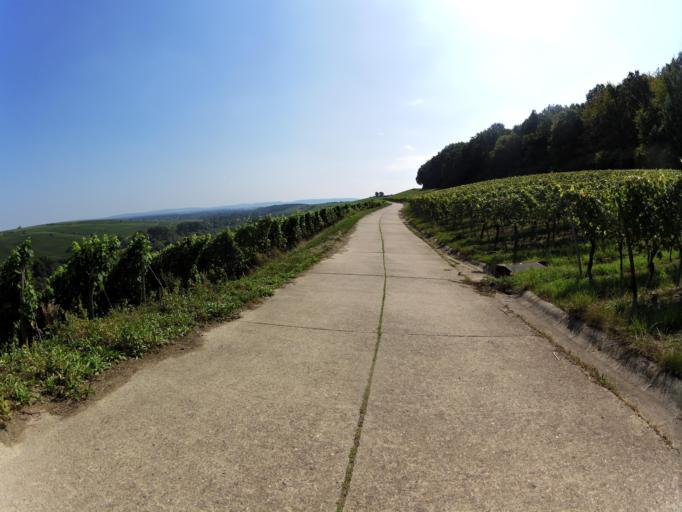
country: DE
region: Bavaria
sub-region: Regierungsbezirk Unterfranken
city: Nordheim
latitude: 49.8441
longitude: 10.1668
